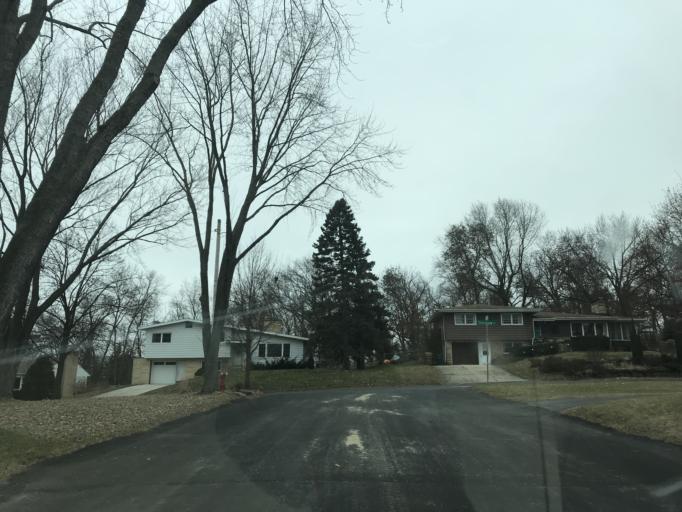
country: US
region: Wisconsin
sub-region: Dane County
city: Monona
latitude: 43.0576
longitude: -89.3220
